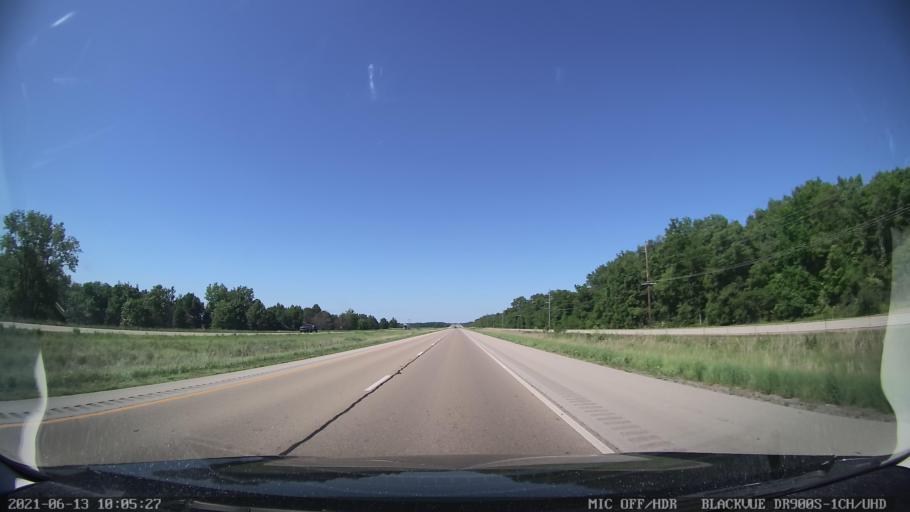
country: US
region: Illinois
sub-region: Logan County
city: Atlanta
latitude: 40.2416
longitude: -89.2549
